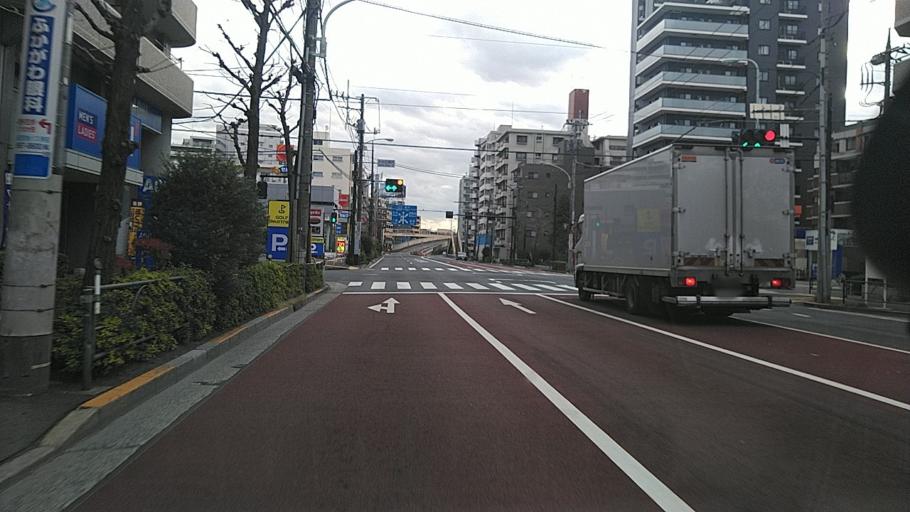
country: JP
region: Saitama
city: Yashio-shi
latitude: 35.7769
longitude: 139.8386
